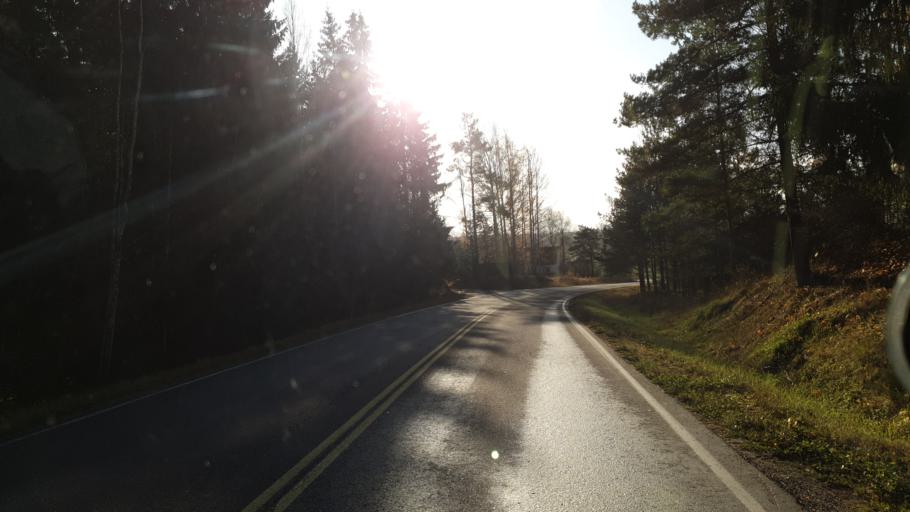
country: FI
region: Uusimaa
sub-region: Helsinki
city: Siuntio
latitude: 60.2159
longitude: 24.1748
